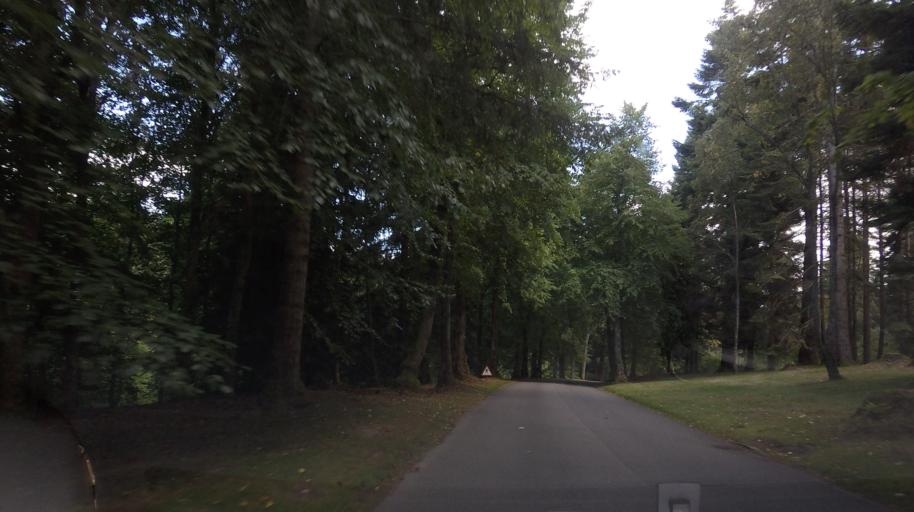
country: GB
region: Scotland
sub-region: Aberdeenshire
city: Banchory
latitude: 57.0592
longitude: -2.4289
